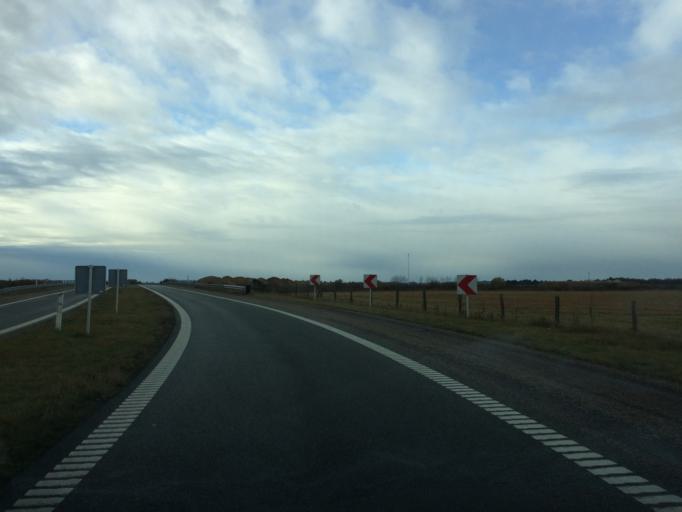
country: DK
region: Central Jutland
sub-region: Herning Kommune
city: Snejbjerg
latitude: 56.1910
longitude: 8.9032
